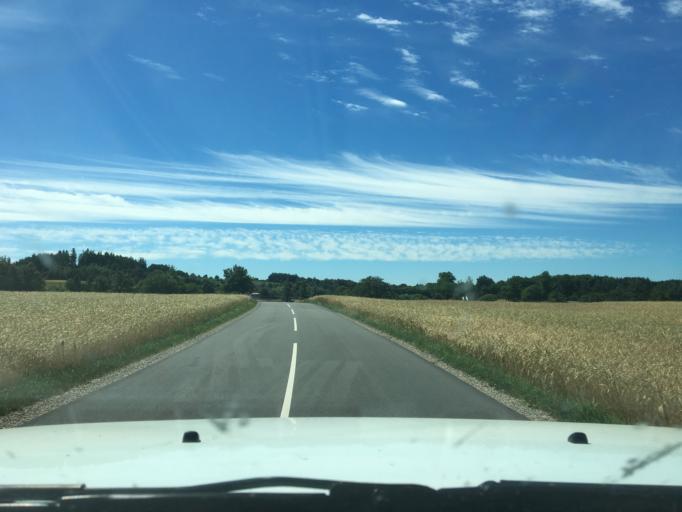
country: DK
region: Central Jutland
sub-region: Syddjurs Kommune
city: Hornslet
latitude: 56.3277
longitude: 10.3685
